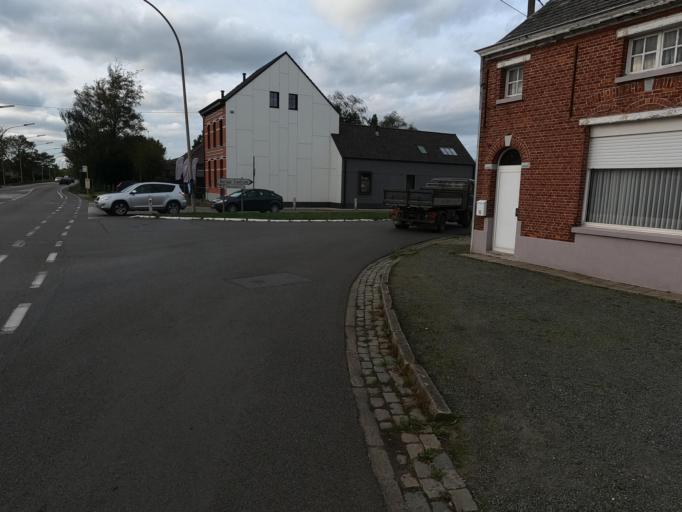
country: BE
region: Flanders
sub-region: Provincie Antwerpen
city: Berlaar
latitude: 51.0849
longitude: 4.6557
